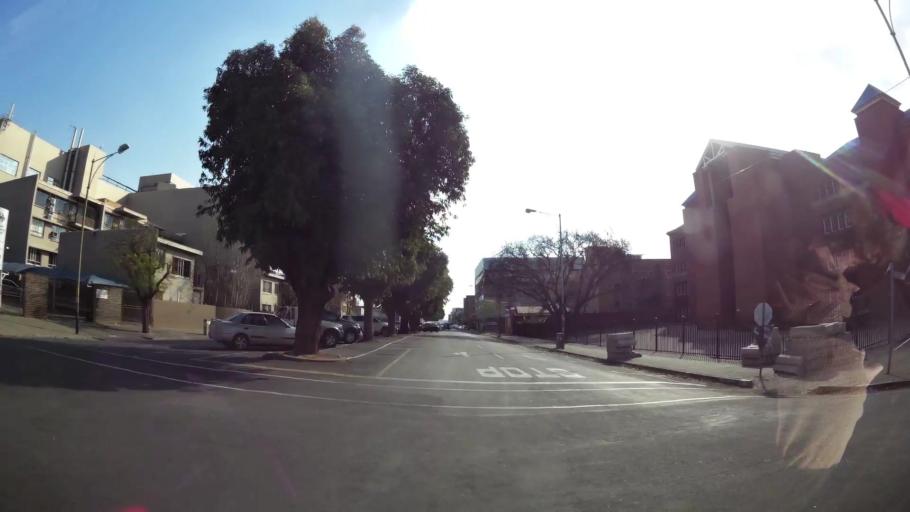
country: ZA
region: Gauteng
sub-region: West Rand District Municipality
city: Krugersdorp
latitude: -26.1045
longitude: 27.7761
